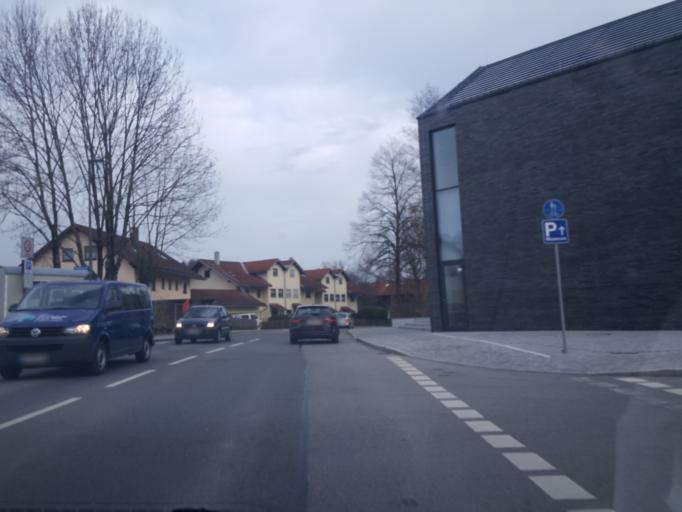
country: DE
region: Bavaria
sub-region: Upper Bavaria
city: Penzberg
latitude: 47.7542
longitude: 11.3720
